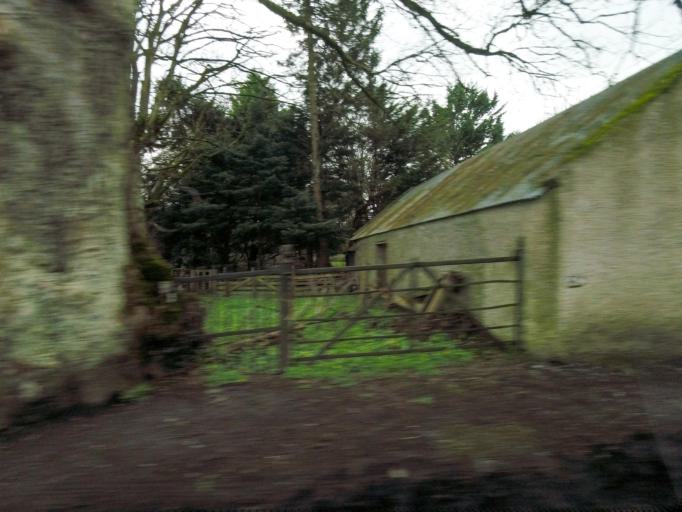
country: IE
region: Leinster
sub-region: Kildare
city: Eadestown
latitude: 53.1689
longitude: -6.6168
